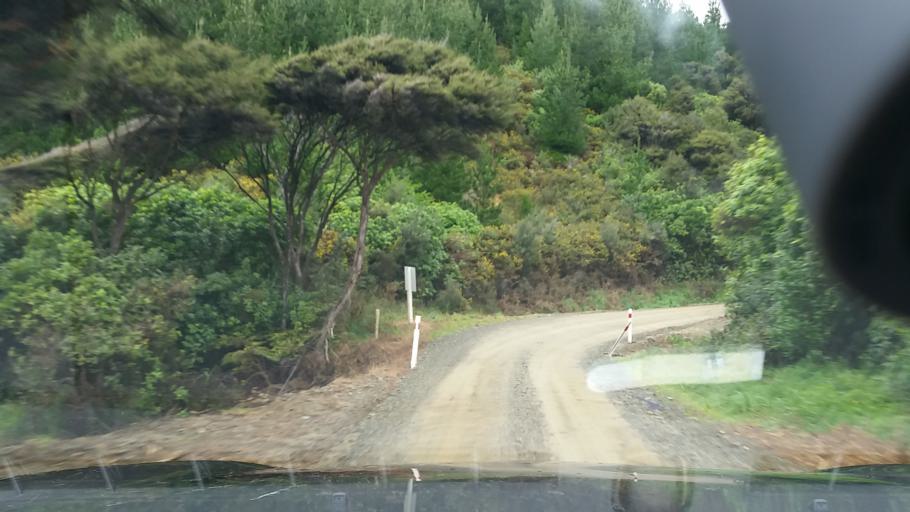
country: NZ
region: Marlborough
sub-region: Marlborough District
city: Picton
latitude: -41.3590
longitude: 174.0706
